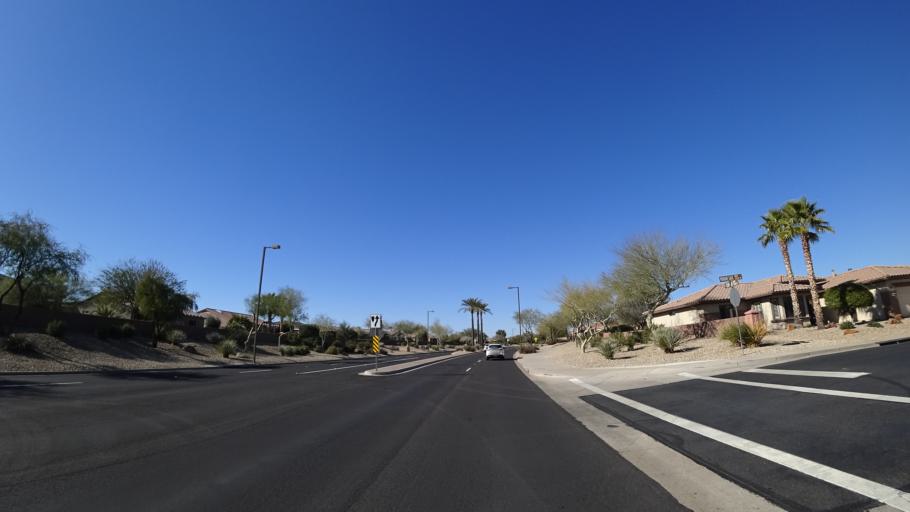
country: US
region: Arizona
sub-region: Maricopa County
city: Sun City West
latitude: 33.6582
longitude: -112.4268
